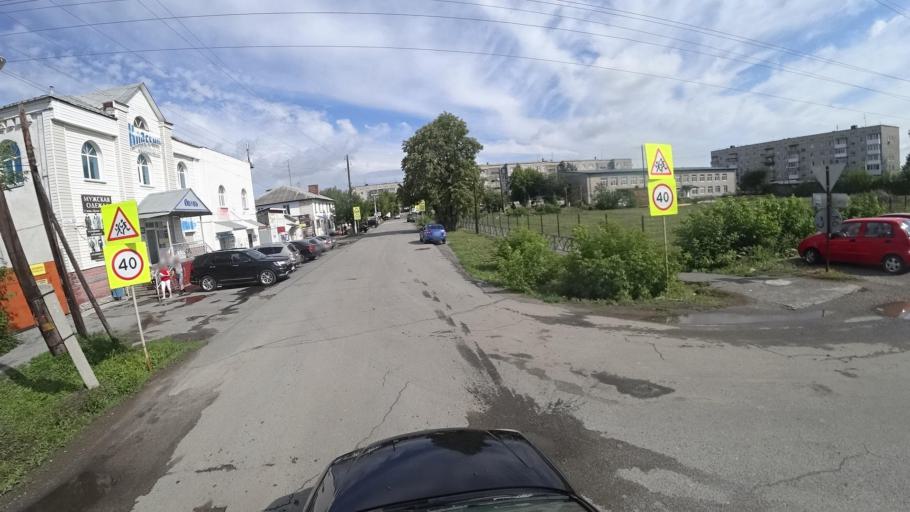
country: RU
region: Sverdlovsk
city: Kamyshlov
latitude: 56.8421
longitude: 62.7118
